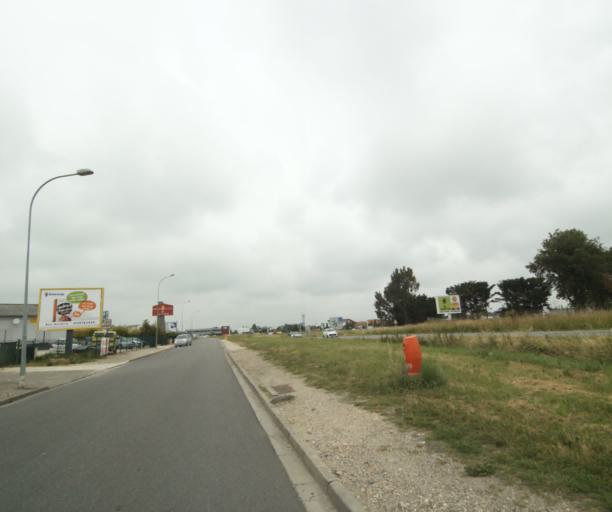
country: FR
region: Midi-Pyrenees
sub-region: Departement du Tarn-et-Garonne
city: Bressols
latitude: 43.9802
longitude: 1.3310
